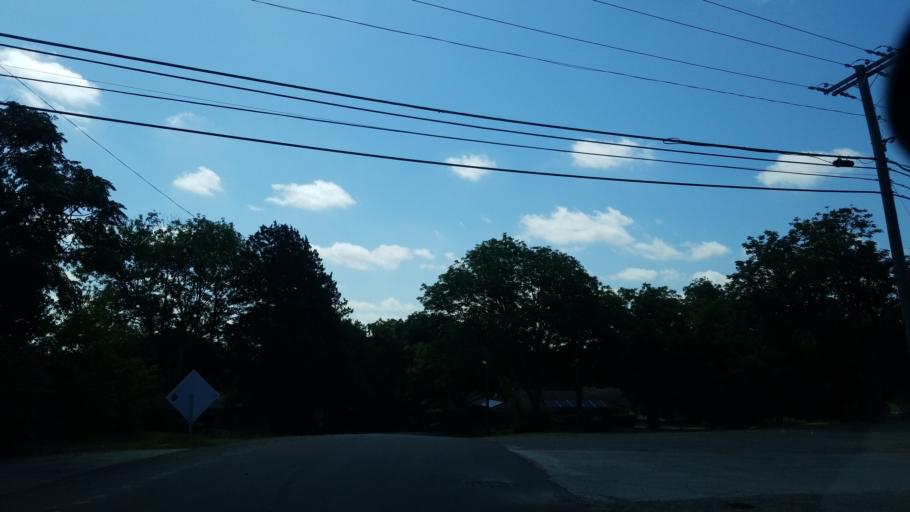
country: US
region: Texas
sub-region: Dallas County
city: Dallas
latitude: 32.7308
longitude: -96.7944
